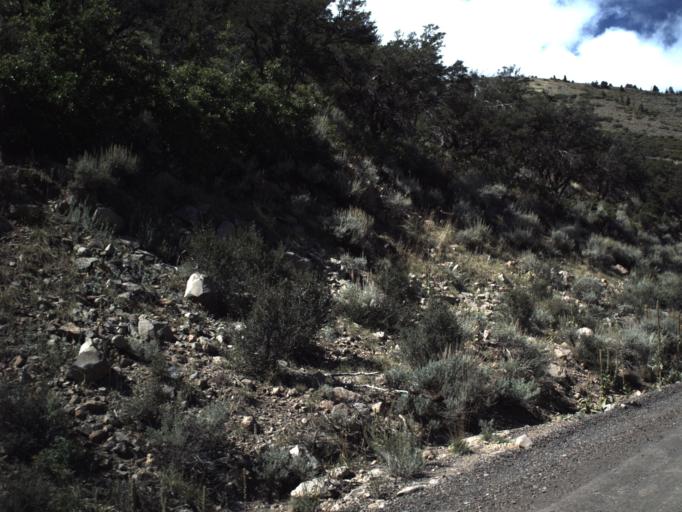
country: US
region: Utah
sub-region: Piute County
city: Junction
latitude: 38.2538
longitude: -112.3143
